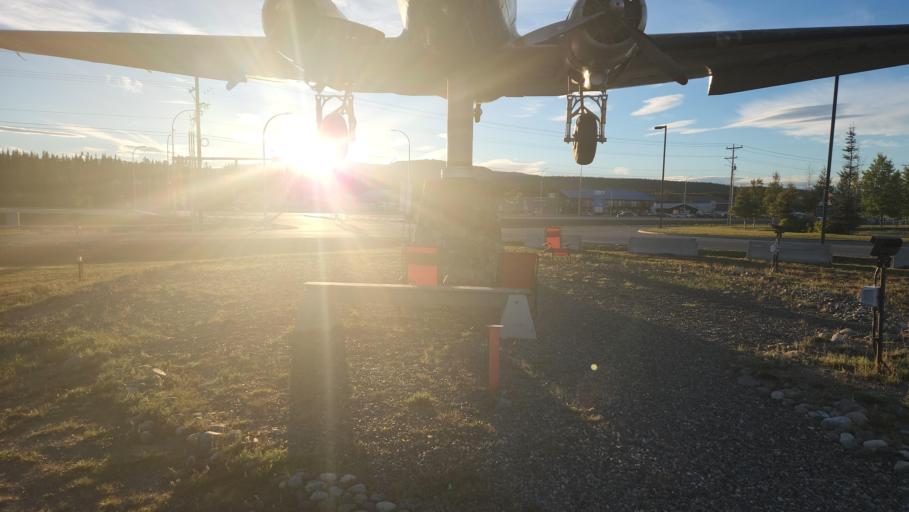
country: CA
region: Yukon
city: Whitehorse
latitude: 60.7120
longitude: -135.0802
